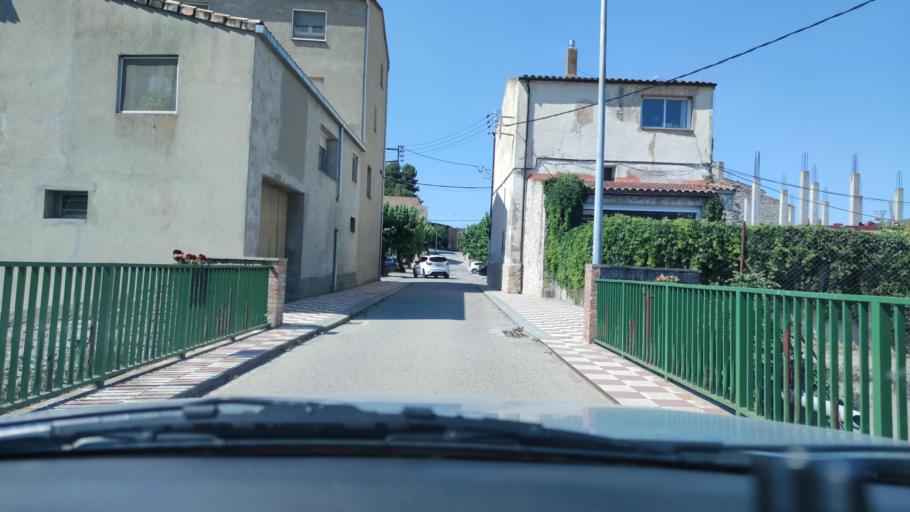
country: ES
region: Catalonia
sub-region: Provincia de Lleida
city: Cervera
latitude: 41.6275
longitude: 1.3421
